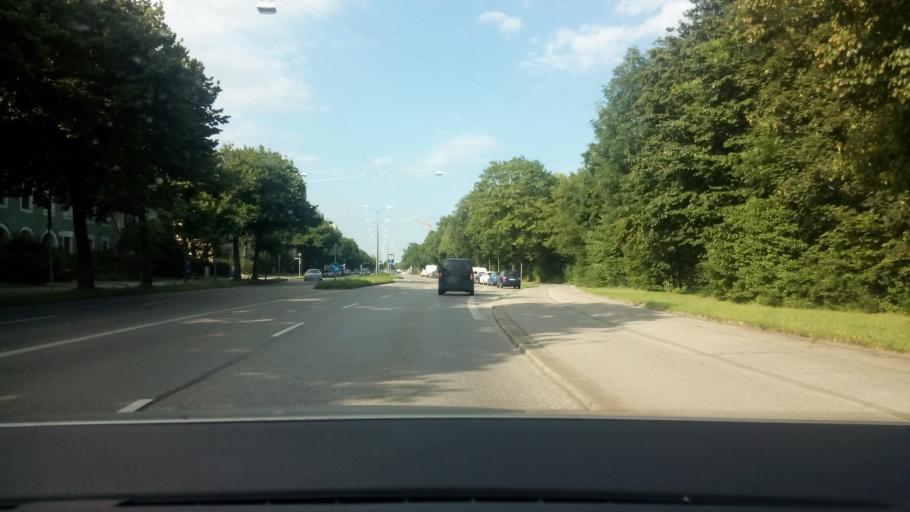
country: DE
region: Bavaria
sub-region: Upper Bavaria
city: Bogenhausen
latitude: 48.1825
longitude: 11.6071
